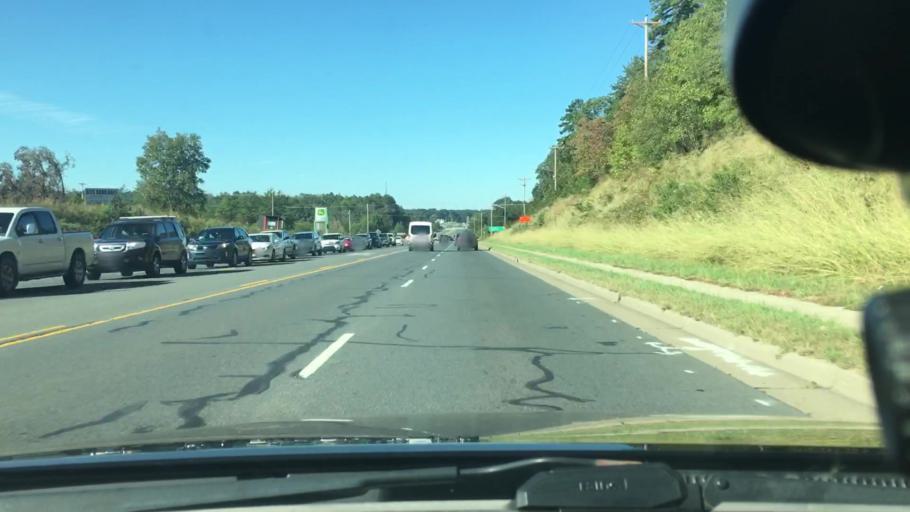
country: US
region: North Carolina
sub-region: Stanly County
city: Albemarle
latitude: 35.3421
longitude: -80.1839
